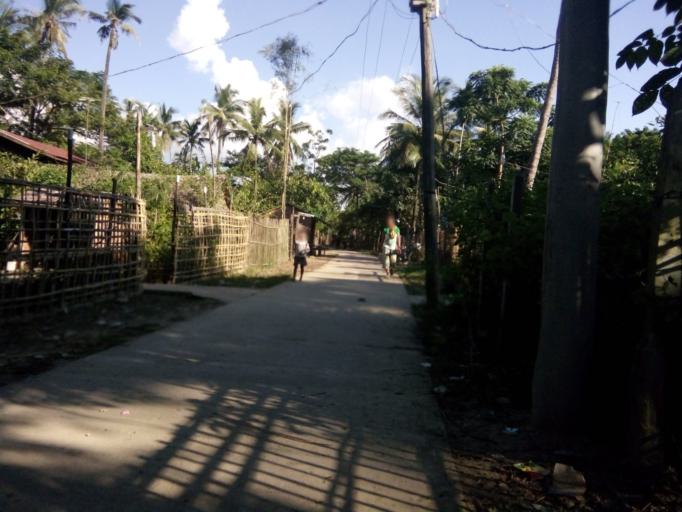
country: MM
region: Yangon
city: Kanbe
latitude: 16.8742
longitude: 95.9788
